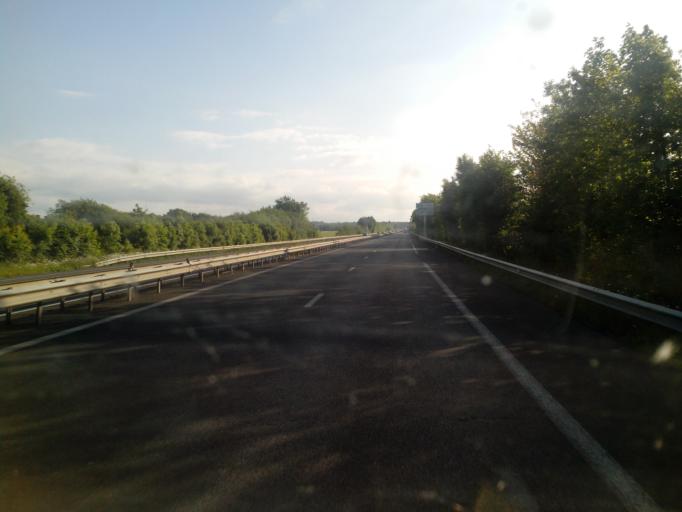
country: FR
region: Lower Normandy
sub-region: Departement du Calvados
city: Grainville-sur-Odon
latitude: 49.1187
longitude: -0.5777
